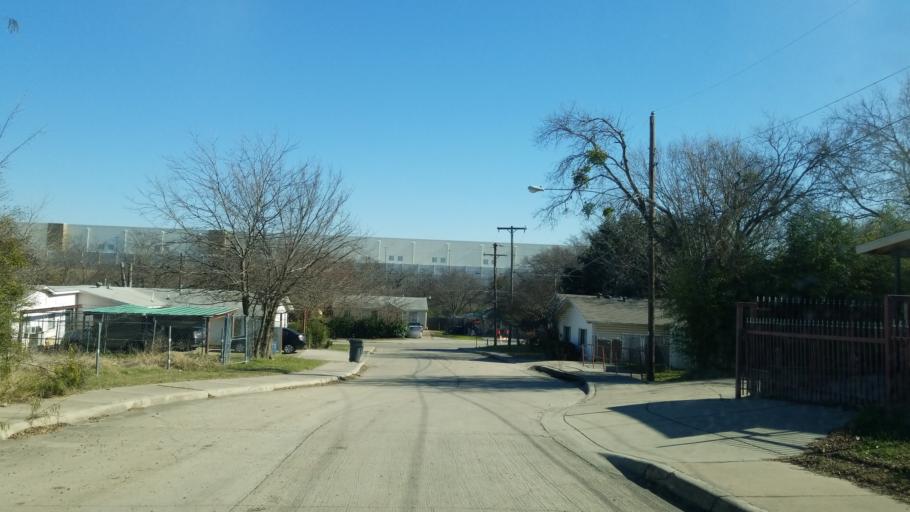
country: US
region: Texas
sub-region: Dallas County
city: Cockrell Hill
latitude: 32.7551
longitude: -96.9087
